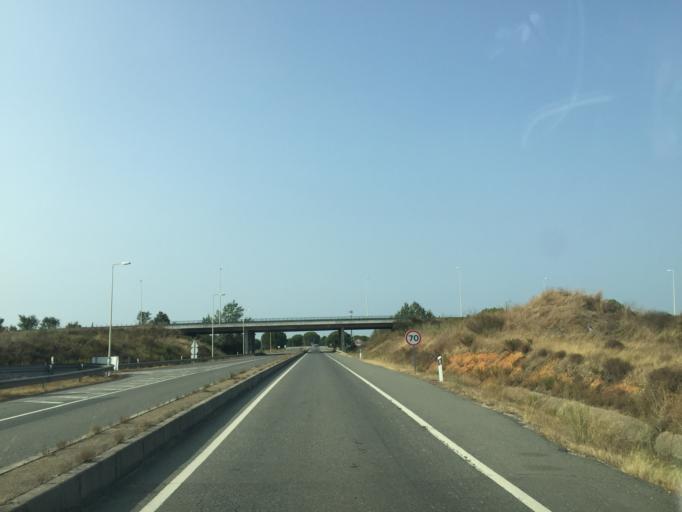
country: PT
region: Setubal
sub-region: Grandola
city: Grandola
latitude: 38.1112
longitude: -8.4182
